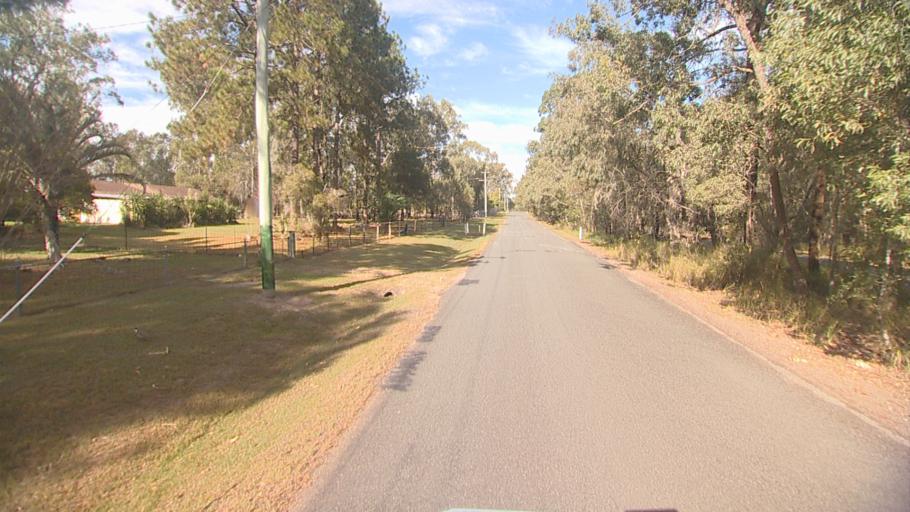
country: AU
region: Queensland
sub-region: Brisbane
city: Forest Lake
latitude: -27.6543
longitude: 152.9831
